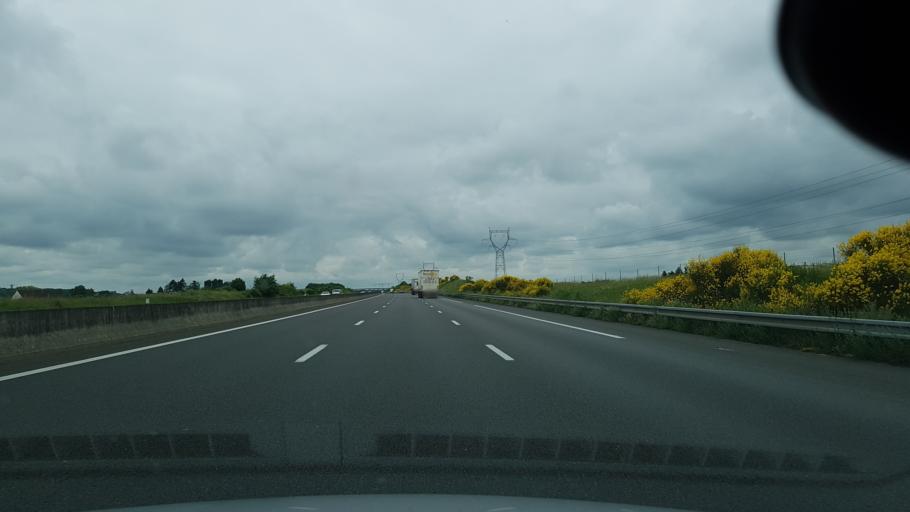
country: FR
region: Centre
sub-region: Departement du Loir-et-Cher
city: Herbault
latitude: 47.6167
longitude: 1.1724
